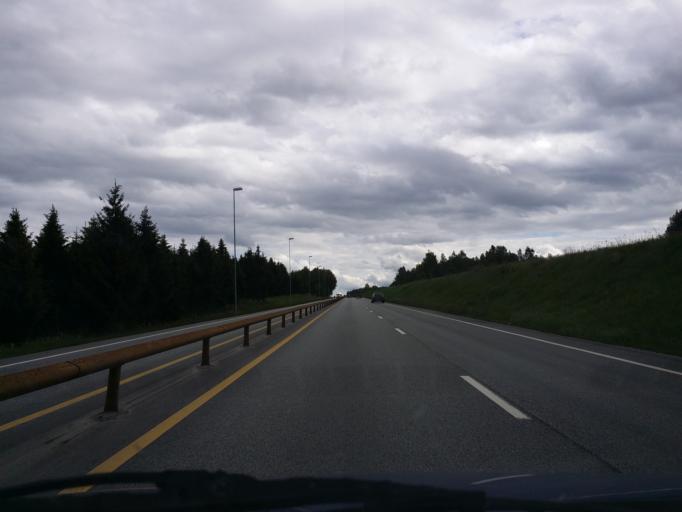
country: NO
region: Hedmark
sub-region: Stange
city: Stange
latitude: 60.7754
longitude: 11.1536
